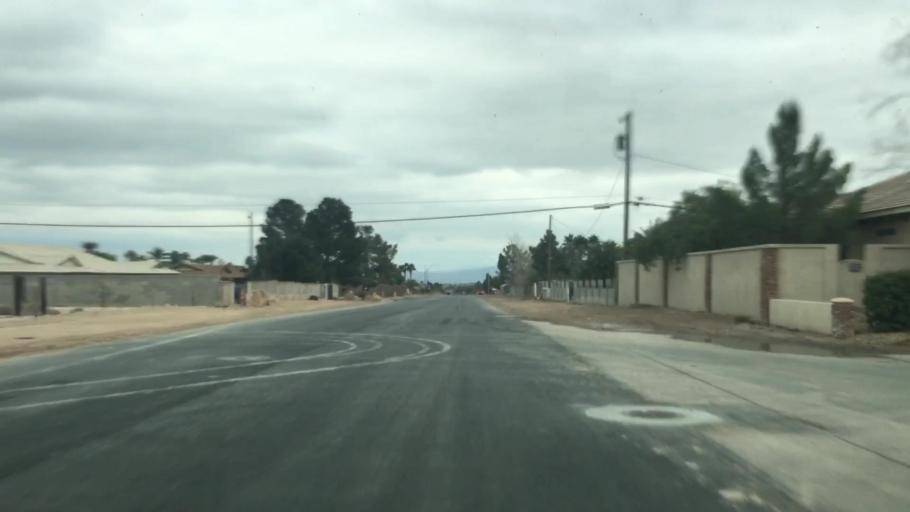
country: US
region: Nevada
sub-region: Clark County
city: Paradise
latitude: 36.0496
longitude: -115.1583
